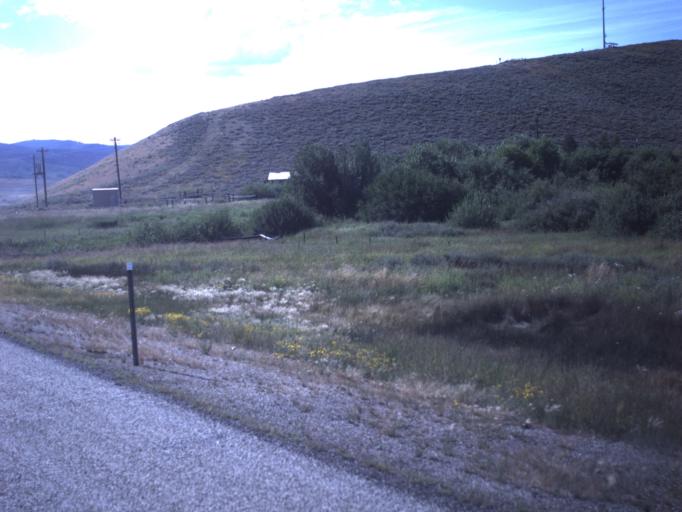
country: US
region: Utah
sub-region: Wasatch County
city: Heber
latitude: 40.2411
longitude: -111.1801
